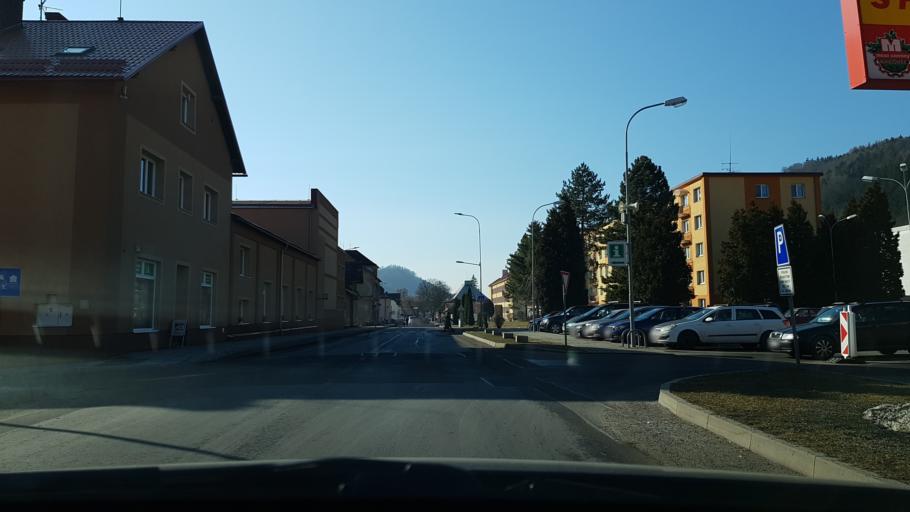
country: CZ
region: Olomoucky
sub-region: Okres Sumperk
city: Hanusovice
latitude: 50.0768
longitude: 16.9326
